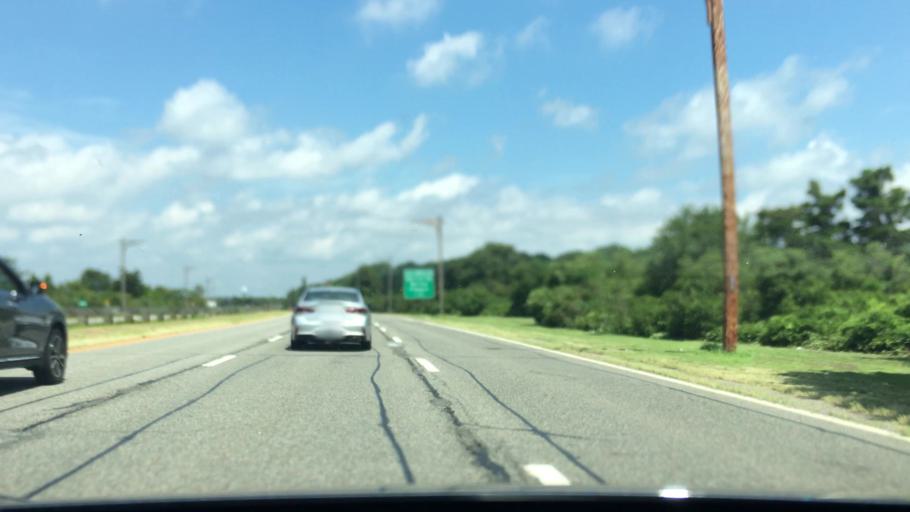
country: US
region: New York
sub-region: Nassau County
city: Merrick
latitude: 40.6370
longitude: -73.5619
